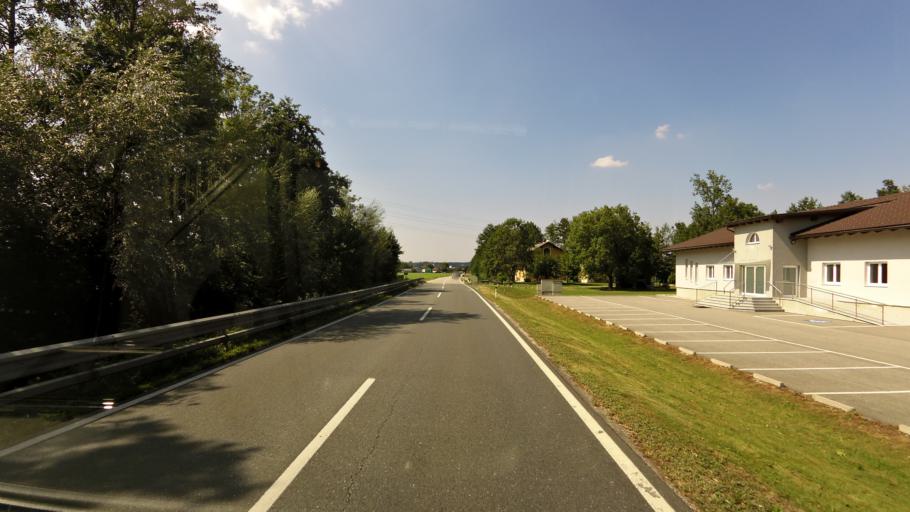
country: AT
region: Upper Austria
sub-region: Politischer Bezirk Braunau am Inn
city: Altheim
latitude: 48.1342
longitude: 13.1423
